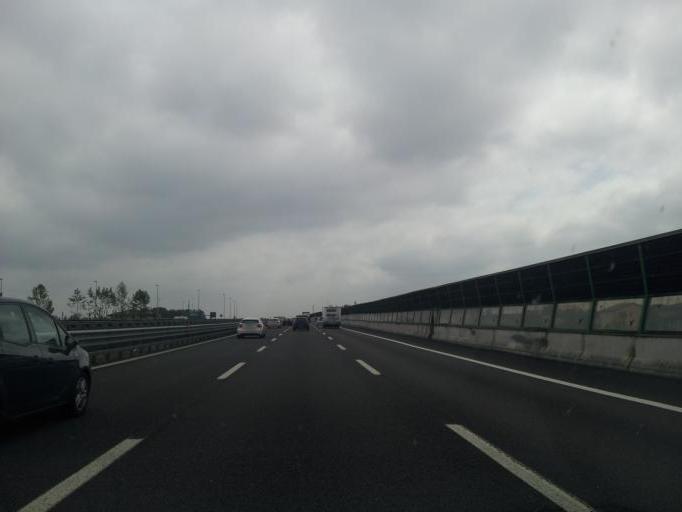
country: IT
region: Veneto
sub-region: Provincia di Vicenza
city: Arcugnano-Torri
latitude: 45.5158
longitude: 11.5627
